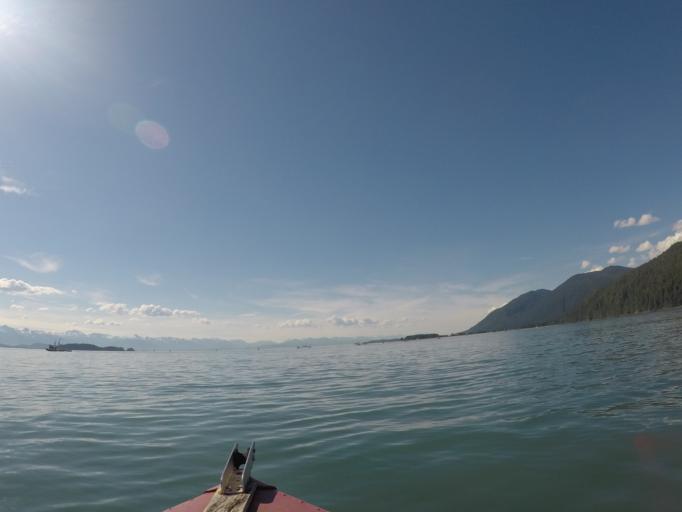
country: US
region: Alaska
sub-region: Juneau City and Borough
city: Juneau
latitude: 58.4949
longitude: -134.8168
